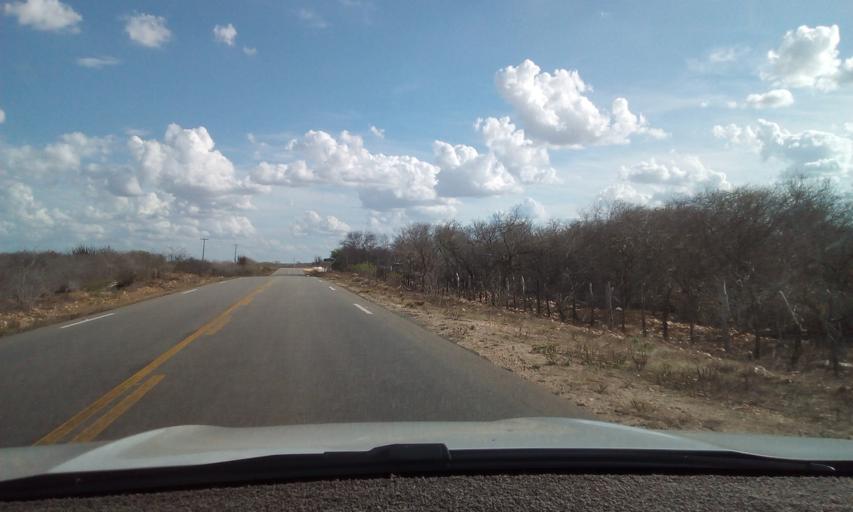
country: BR
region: Paraiba
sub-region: Soledade
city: Soledade
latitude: -6.8171
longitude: -36.4048
